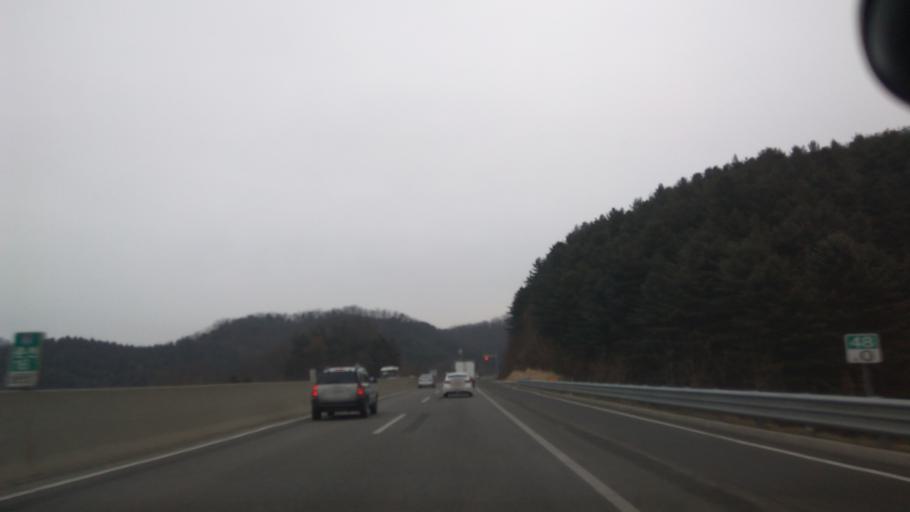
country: KR
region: Gangwon-do
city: Sindong
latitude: 37.7376
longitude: 127.6322
